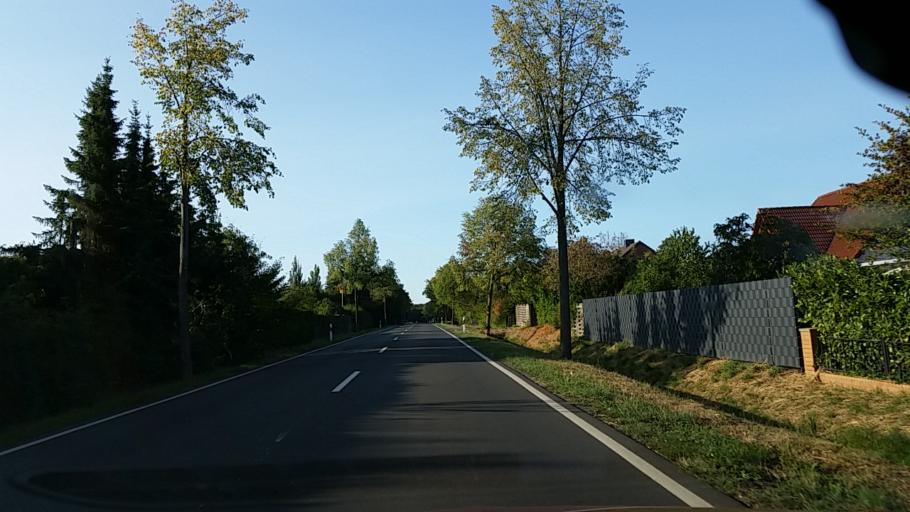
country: DE
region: Lower Saxony
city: Lehre
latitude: 52.2945
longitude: 10.6558
